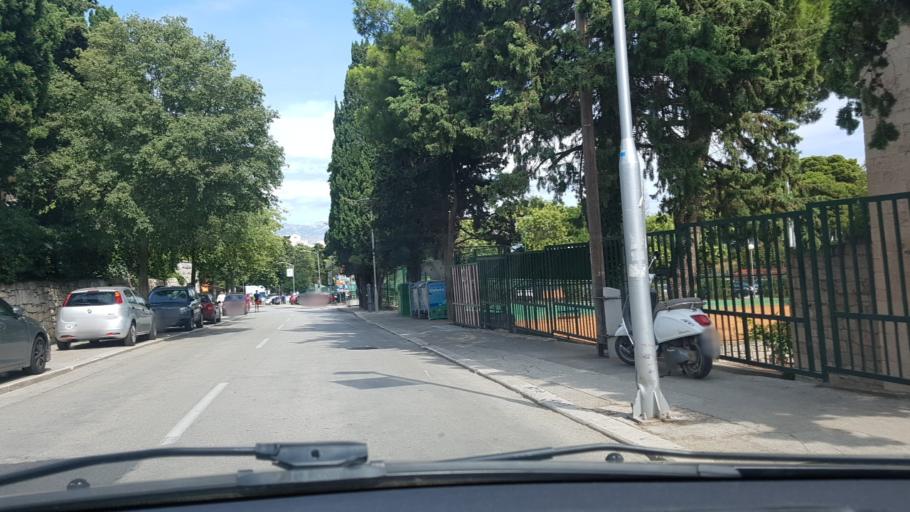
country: HR
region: Splitsko-Dalmatinska
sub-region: Grad Split
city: Split
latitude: 43.5013
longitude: 16.4541
